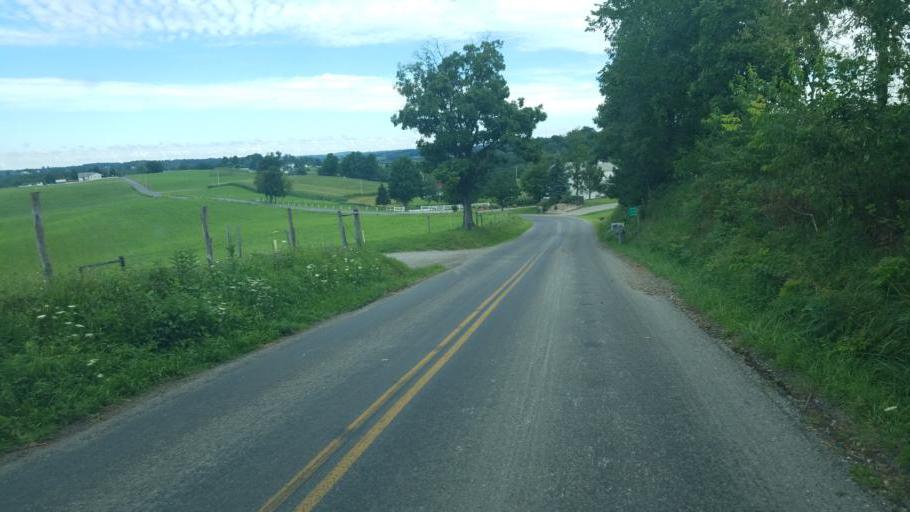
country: US
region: Ohio
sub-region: Holmes County
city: Millersburg
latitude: 40.4957
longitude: -81.7943
